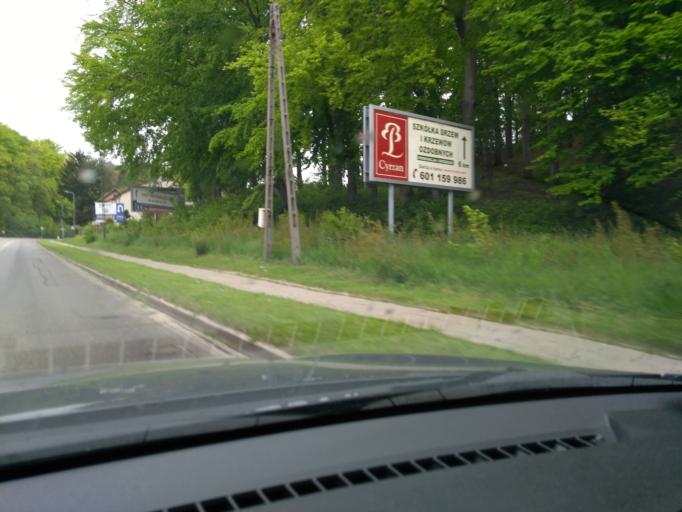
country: PL
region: Pomeranian Voivodeship
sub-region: Powiat kartuski
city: Kartuzy
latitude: 54.3384
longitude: 18.1853
